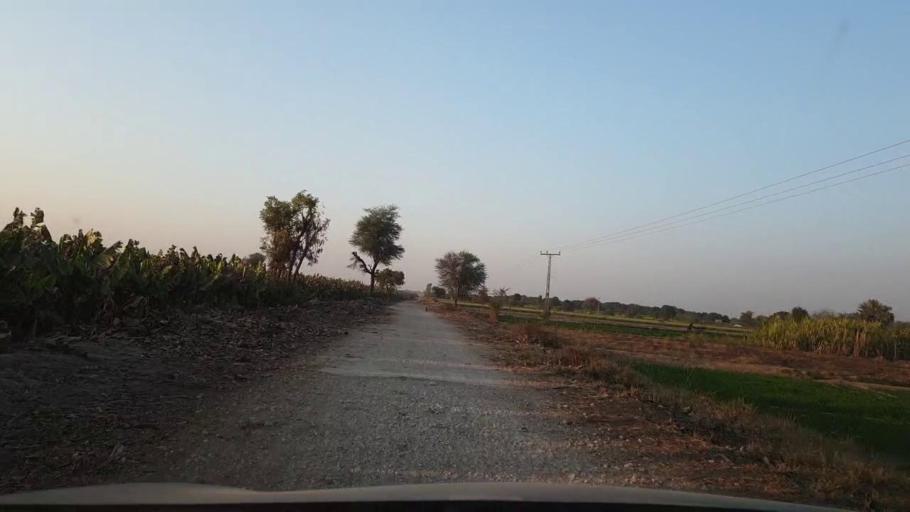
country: PK
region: Sindh
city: Tando Allahyar
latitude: 25.5154
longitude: 68.7389
